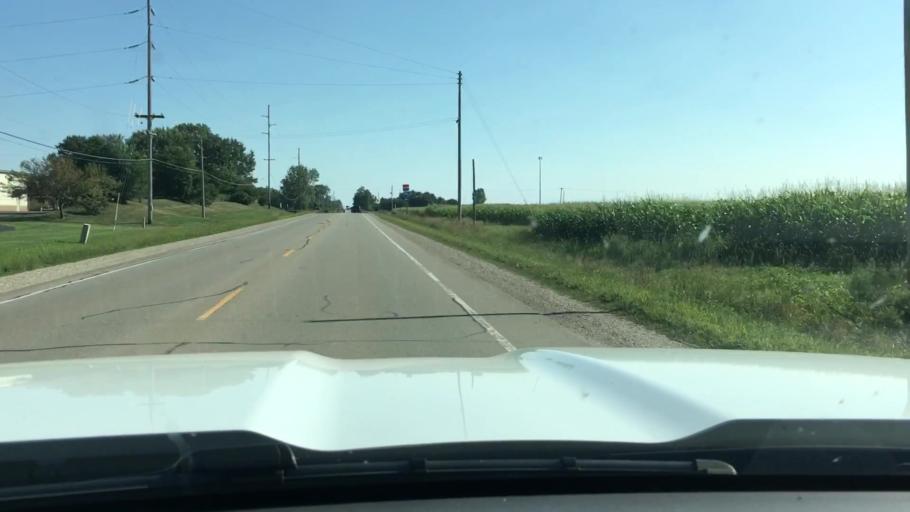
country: US
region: Michigan
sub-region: Ottawa County
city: Coopersville
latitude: 43.0479
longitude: -85.9568
